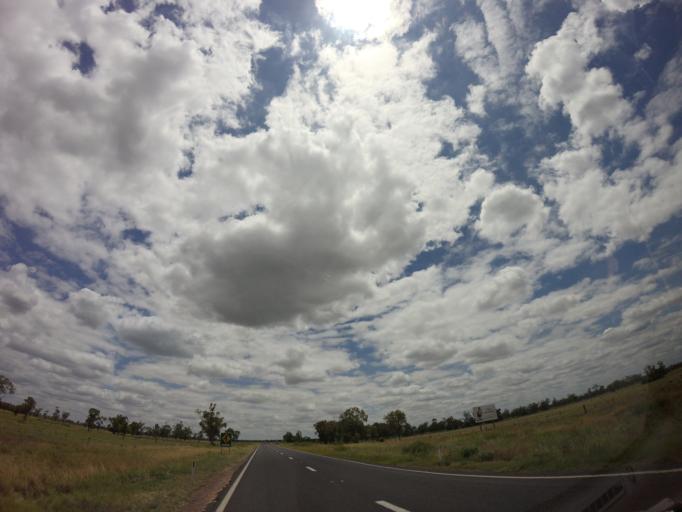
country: AU
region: New South Wales
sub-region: Moree Plains
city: Boggabilla
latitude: -28.6302
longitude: 150.3451
